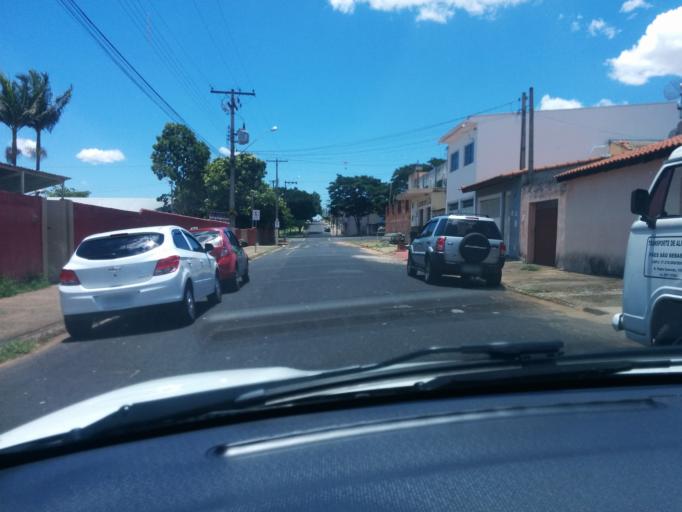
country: BR
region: Sao Paulo
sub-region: Franca
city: Franca
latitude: -20.5750
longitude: -47.3729
